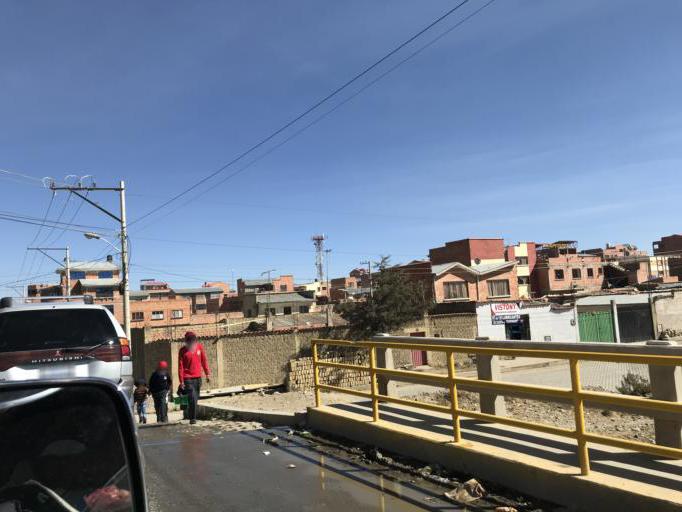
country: BO
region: La Paz
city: La Paz
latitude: -16.4862
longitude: -68.2009
